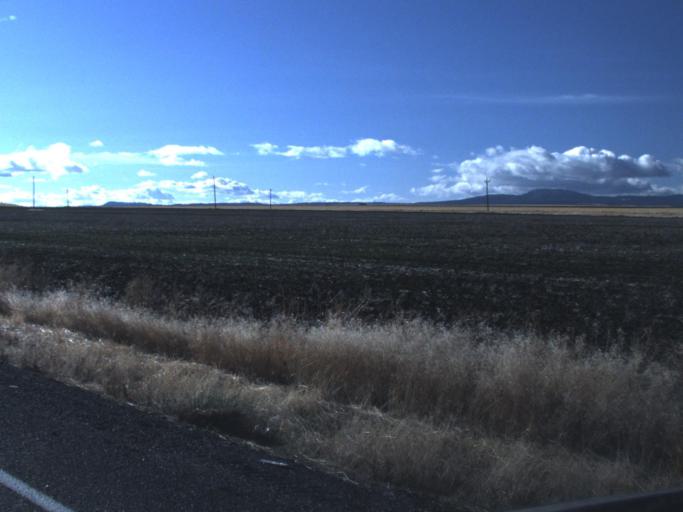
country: US
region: Washington
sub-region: Asotin County
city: Asotin
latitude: 46.2189
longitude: -117.0703
